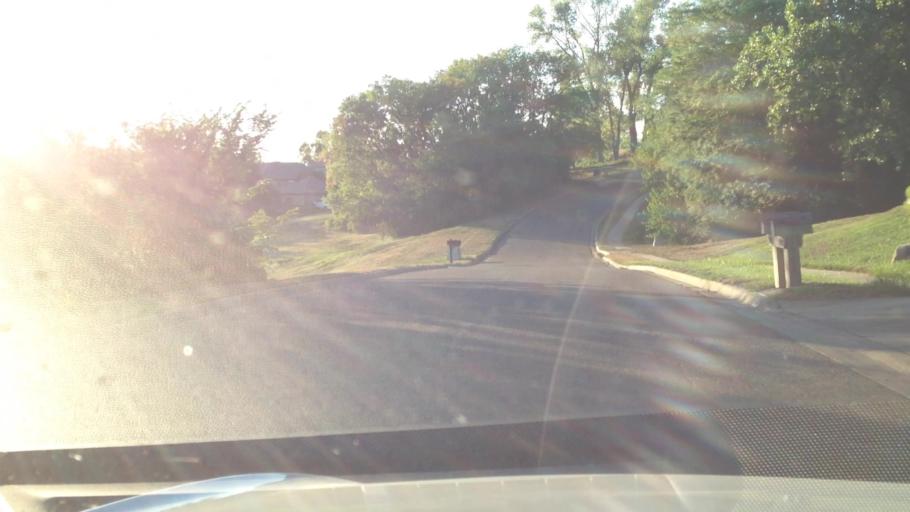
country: US
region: Kansas
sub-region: Douglas County
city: Lawrence
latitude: 38.9489
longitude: -95.2907
